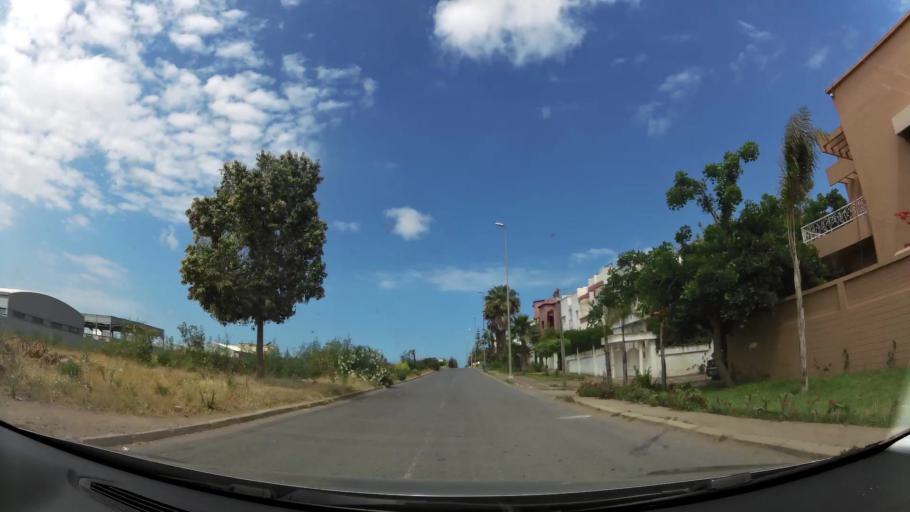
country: MA
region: Gharb-Chrarda-Beni Hssen
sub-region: Kenitra Province
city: Kenitra
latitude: 34.2414
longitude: -6.6040
